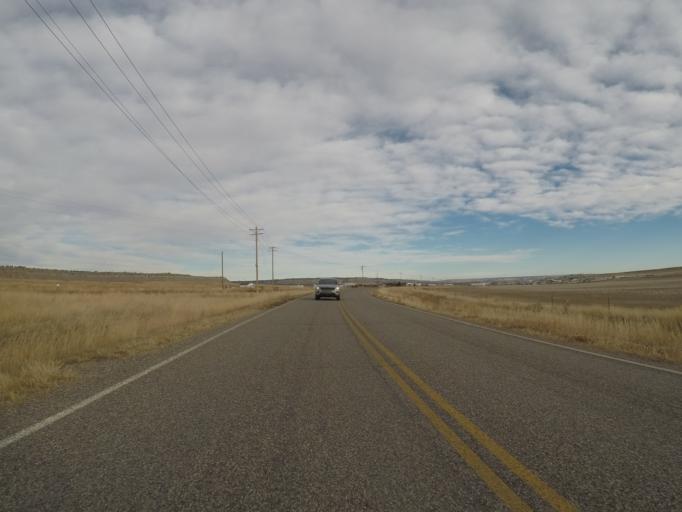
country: US
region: Montana
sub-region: Yellowstone County
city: Laurel
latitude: 45.7836
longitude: -108.7302
